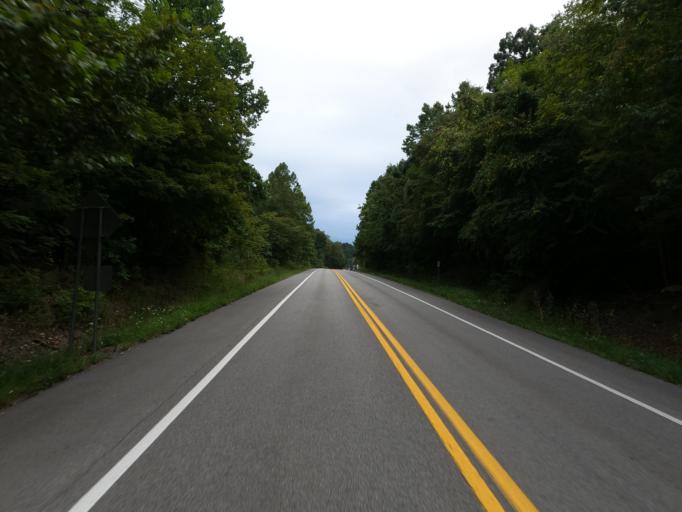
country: US
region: West Virginia
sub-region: Marion County
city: Fairmont
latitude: 39.4939
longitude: -80.0910
